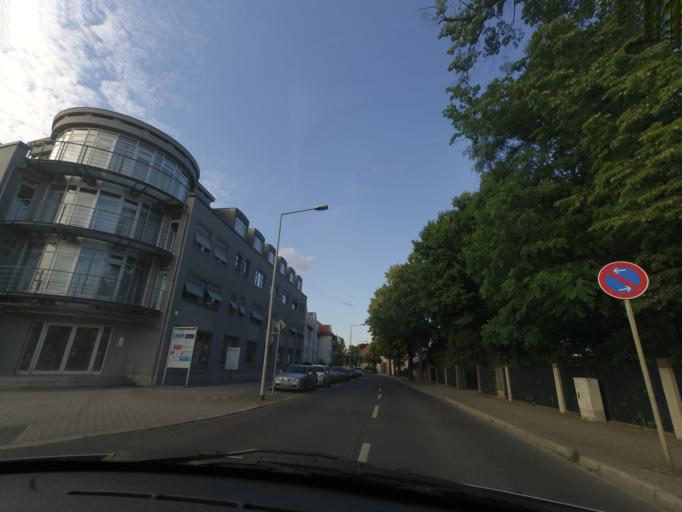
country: DE
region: Saxony
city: Heidenau
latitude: 50.9962
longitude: 13.8211
